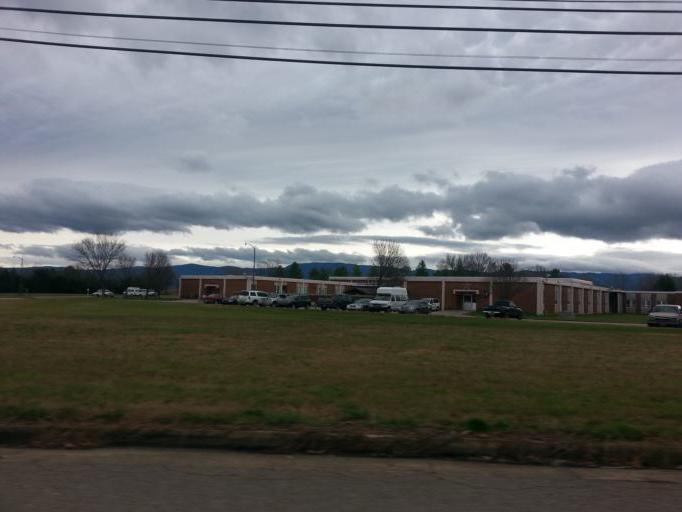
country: US
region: Tennessee
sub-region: Greene County
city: Tusculum
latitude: 36.1854
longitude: -82.7405
